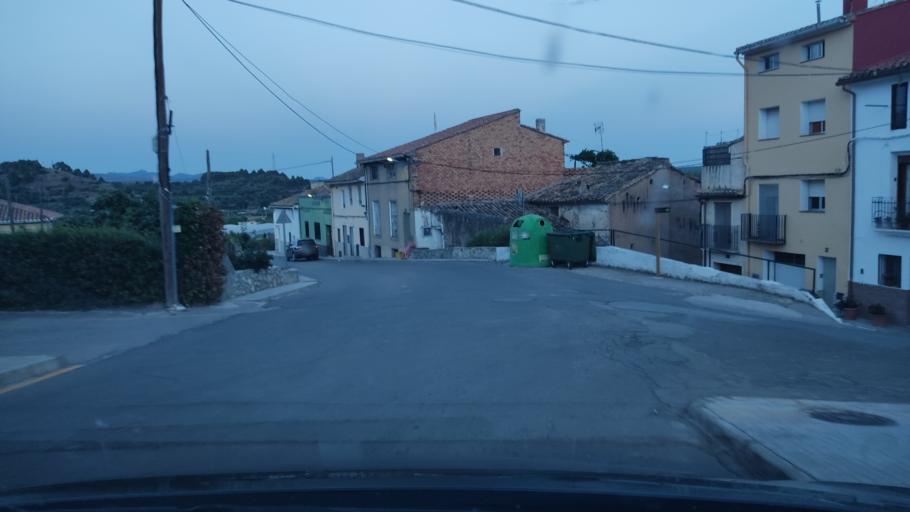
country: ES
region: Valencia
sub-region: Provincia de Castello
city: Jerica
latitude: 39.9100
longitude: -0.5697
